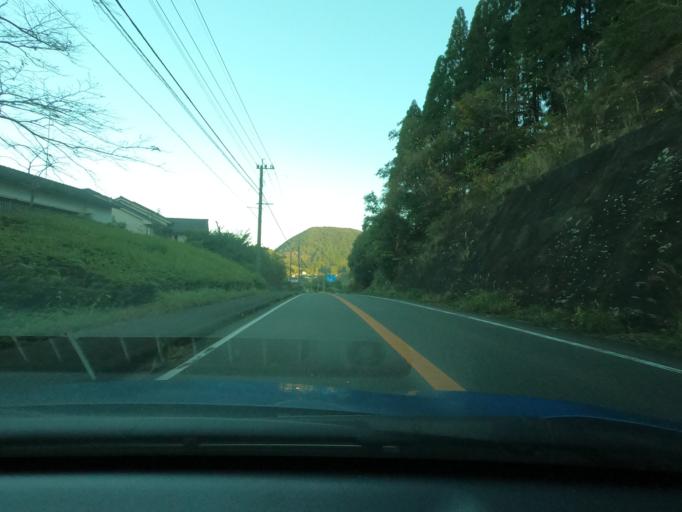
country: JP
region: Kagoshima
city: Satsumasendai
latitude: 31.8055
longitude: 130.3930
